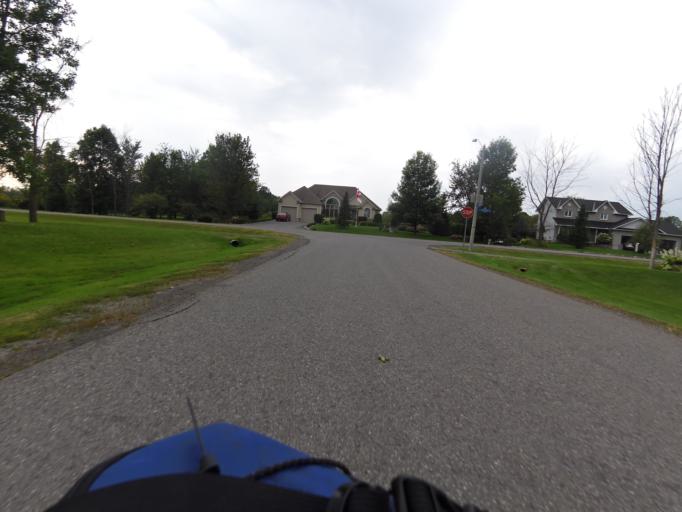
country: CA
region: Ontario
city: Ottawa
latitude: 45.2253
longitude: -75.4797
